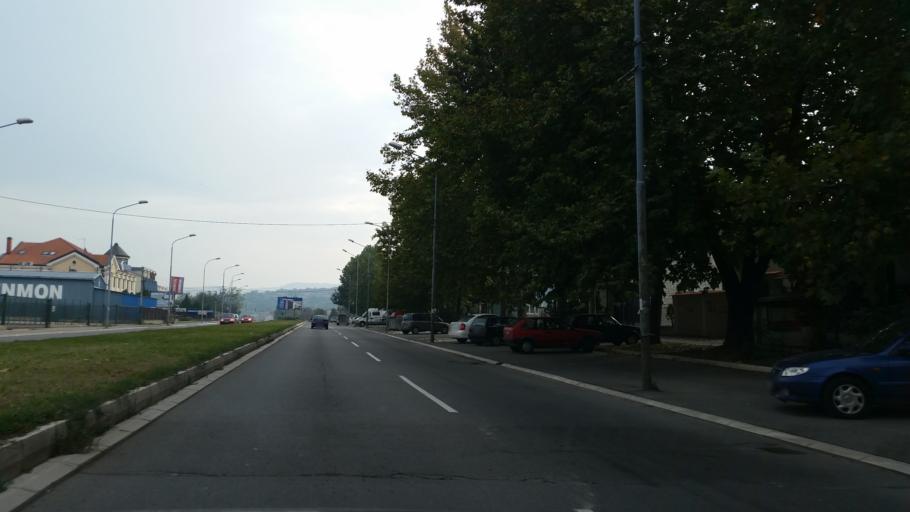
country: RS
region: Central Serbia
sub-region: Belgrade
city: Palilula
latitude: 44.8175
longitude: 20.5168
